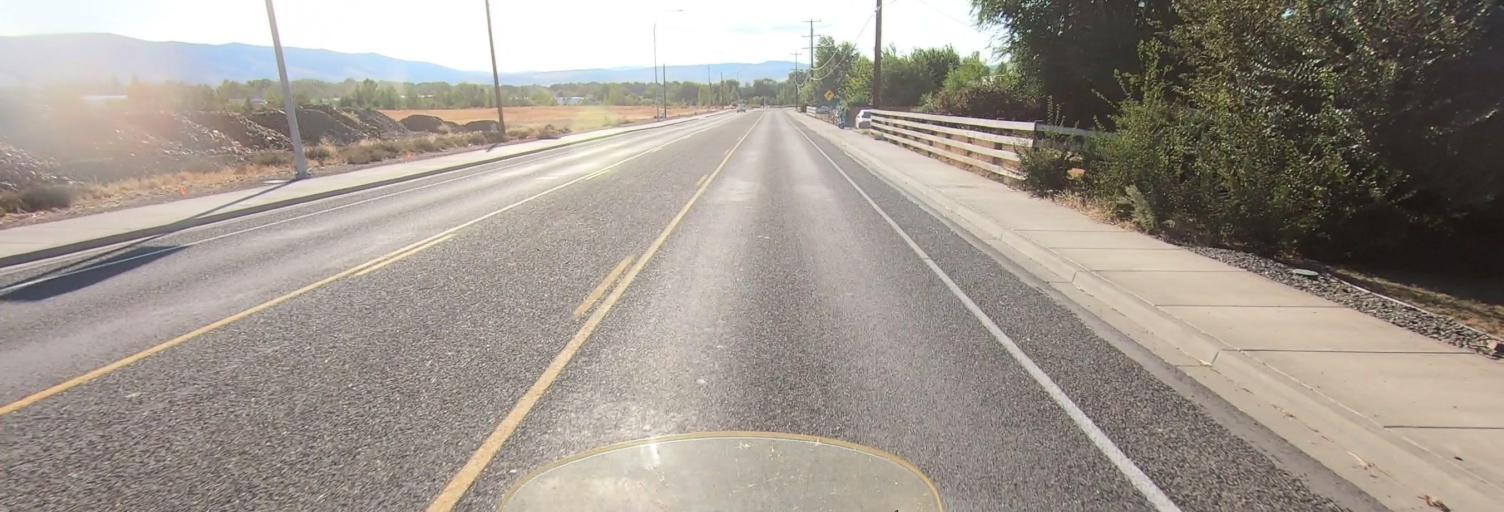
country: US
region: Washington
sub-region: Kittitas County
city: Ellensburg
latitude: 46.9997
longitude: -120.5696
